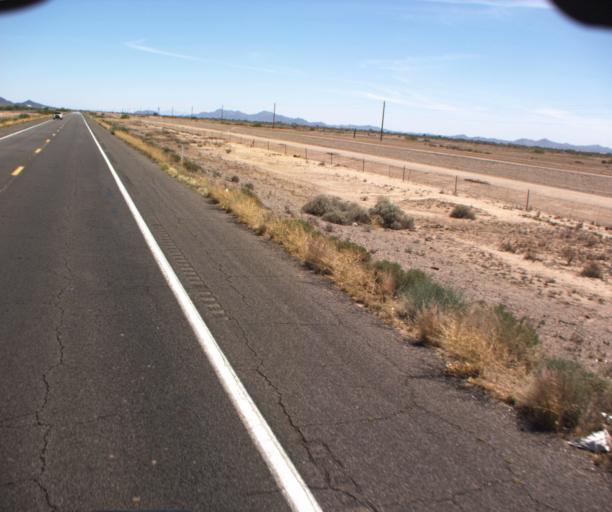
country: US
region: Arizona
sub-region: Maricopa County
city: Sun Lakes
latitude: 33.1873
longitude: -111.8134
